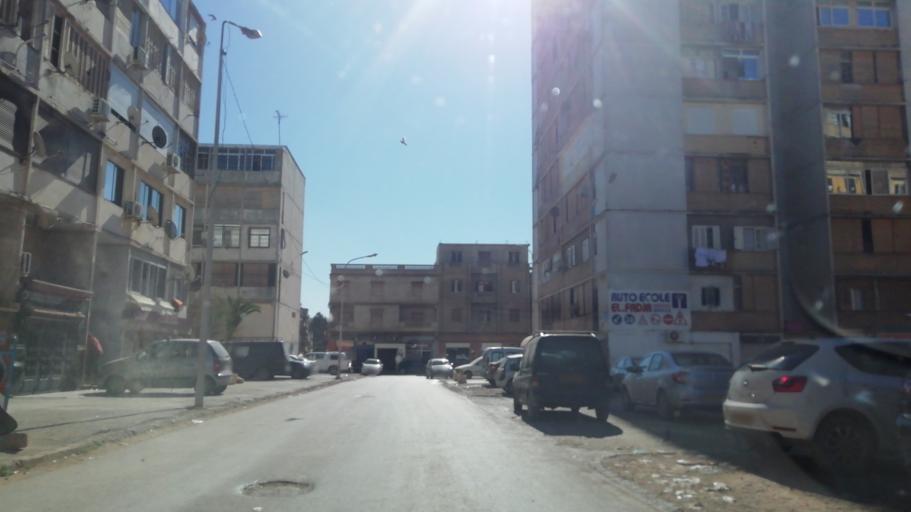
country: DZ
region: Oran
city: Oran
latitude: 35.6909
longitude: -0.6118
